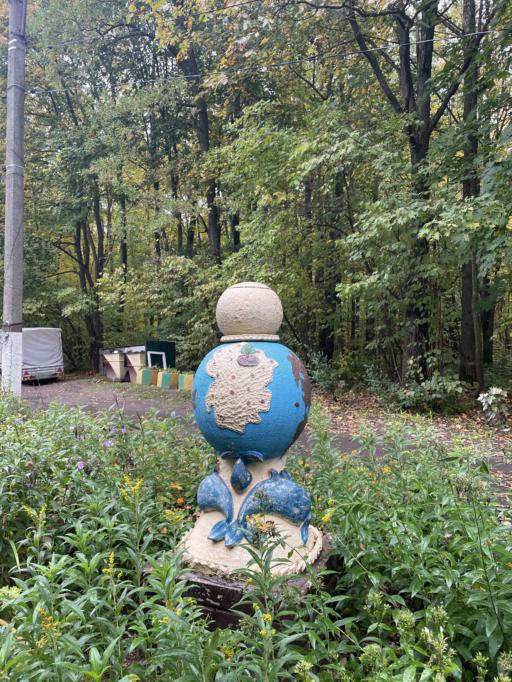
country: RU
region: Chuvashia
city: Novocheboksarsk
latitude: 56.1202
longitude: 47.4694
